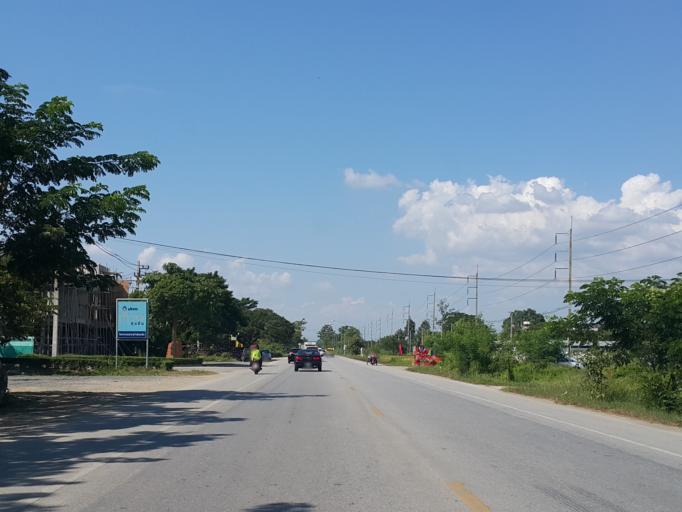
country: TH
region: Chiang Mai
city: San Sai
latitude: 18.8109
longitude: 99.0570
